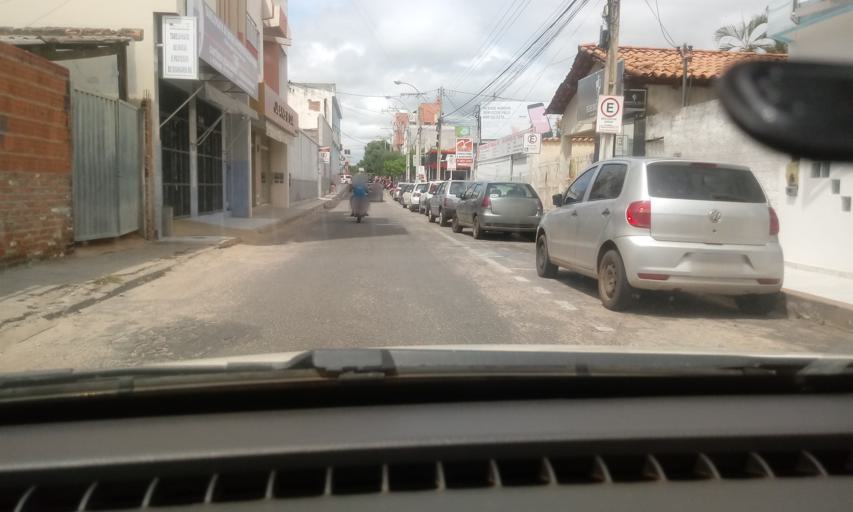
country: BR
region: Bahia
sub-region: Guanambi
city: Guanambi
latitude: -14.2246
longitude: -42.7787
